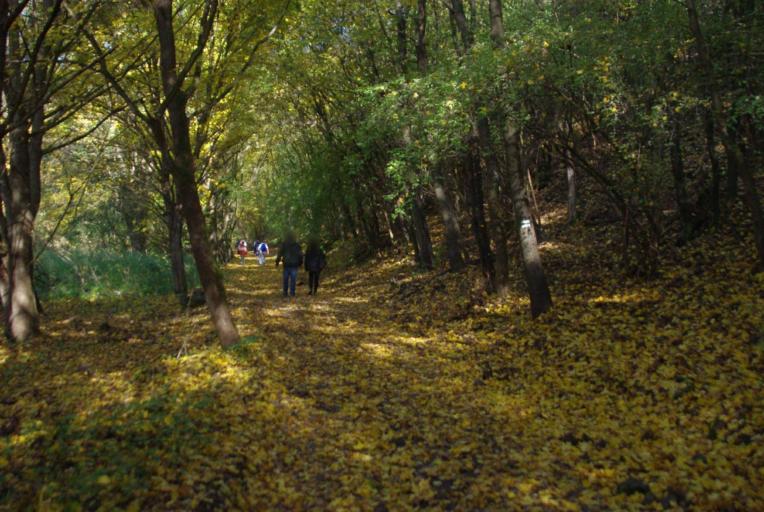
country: HU
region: Pest
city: Szob
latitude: 47.8235
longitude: 18.9156
